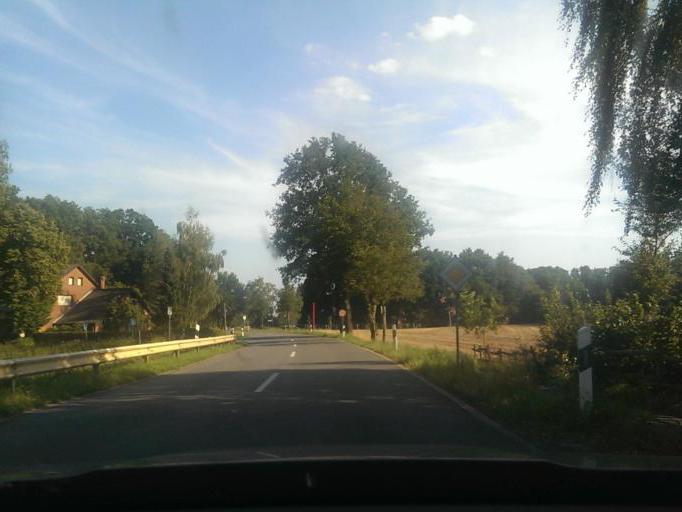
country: DE
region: North Rhine-Westphalia
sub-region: Regierungsbezirk Detmold
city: Delbruck
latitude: 51.7403
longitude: 8.5947
